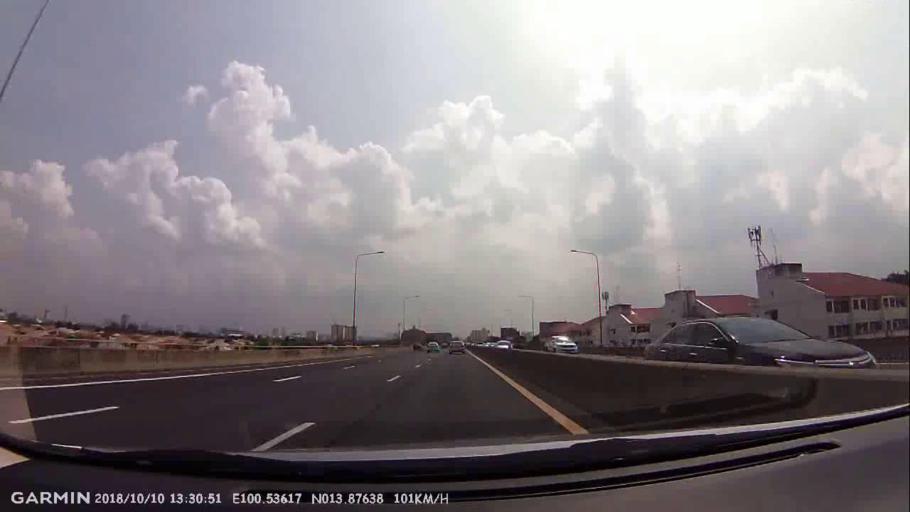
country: TH
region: Nonthaburi
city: Mueang Nonthaburi
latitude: 13.8762
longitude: 100.5361
